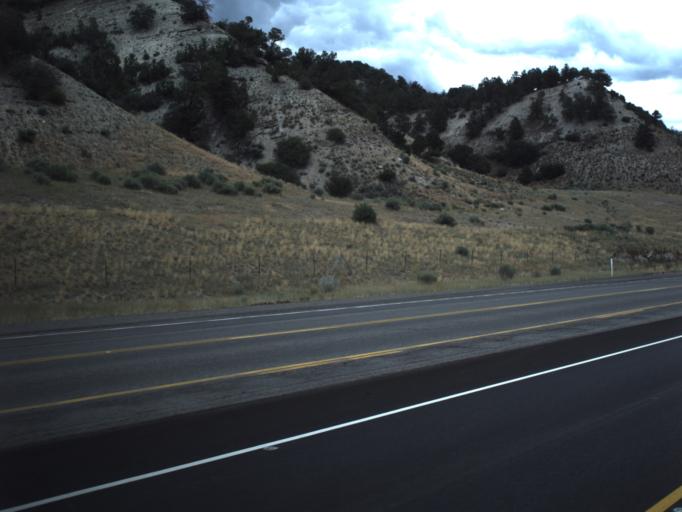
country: US
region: Utah
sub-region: Utah County
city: Mapleton
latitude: 39.9568
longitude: -111.3009
